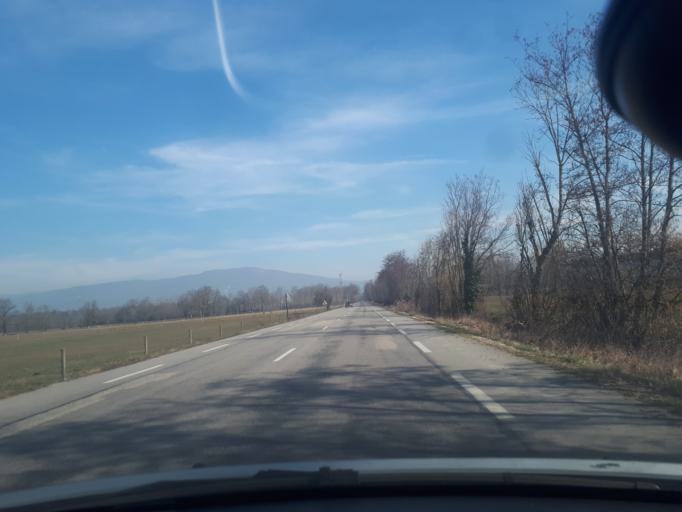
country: FR
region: Rhone-Alpes
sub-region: Departement de l'Isere
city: Morestel
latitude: 45.6736
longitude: 5.4833
